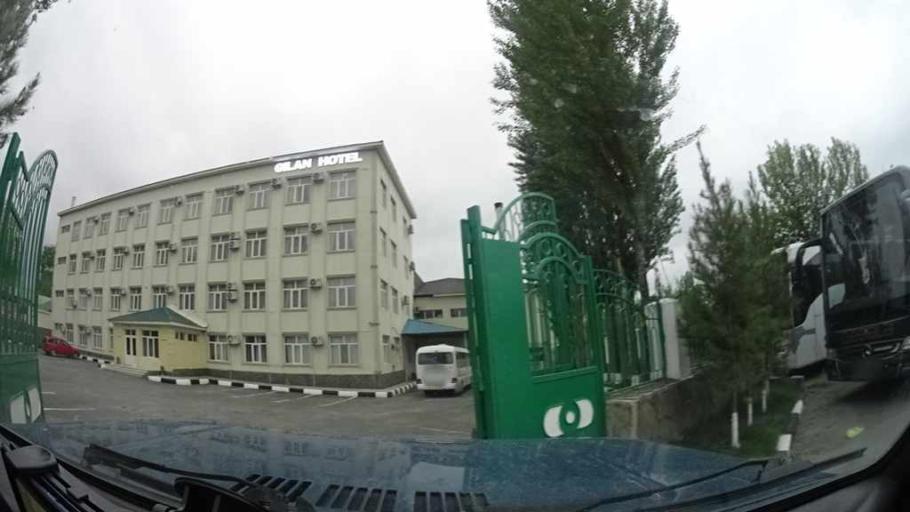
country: AZ
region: Qabala Rayon
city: Qutqashen
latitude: 40.9478
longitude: 47.8222
